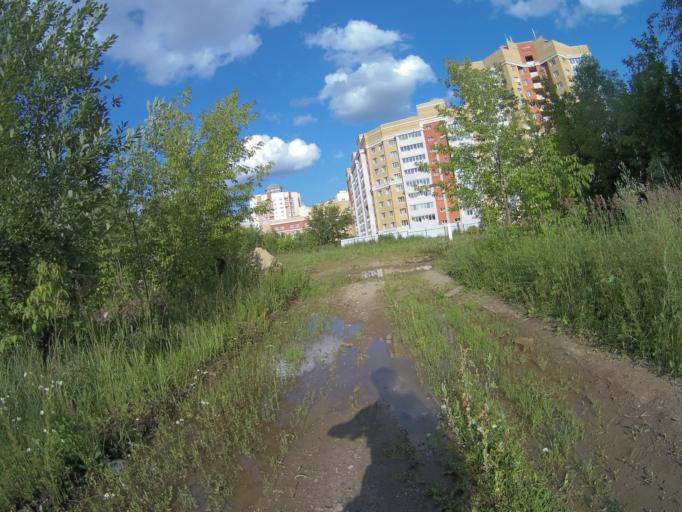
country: RU
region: Vladimir
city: Vladimir
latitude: 56.1382
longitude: 40.3821
